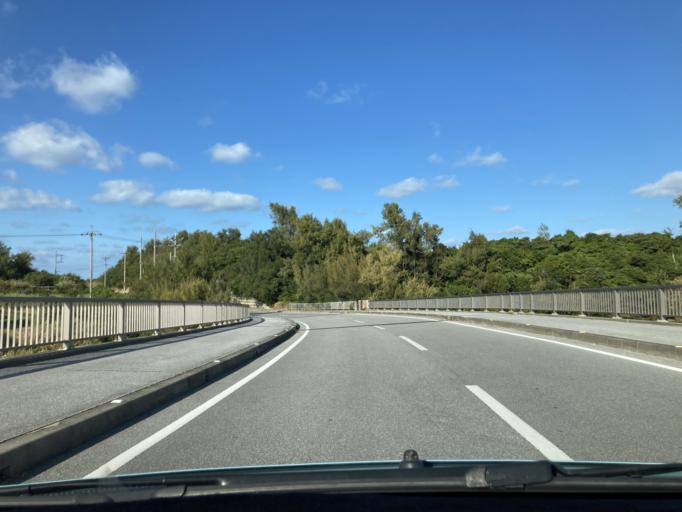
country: JP
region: Okinawa
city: Katsuren-haebaru
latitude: 26.3166
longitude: 127.9183
